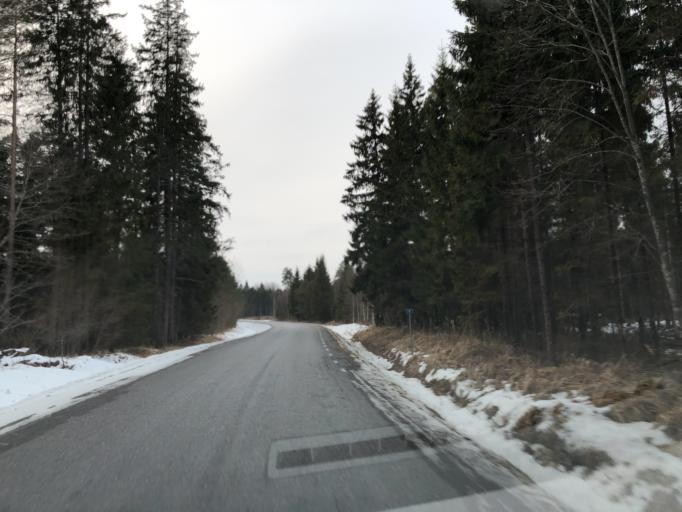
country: EE
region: Paernumaa
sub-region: Vaendra vald (alev)
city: Vandra
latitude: 58.6934
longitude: 24.9744
